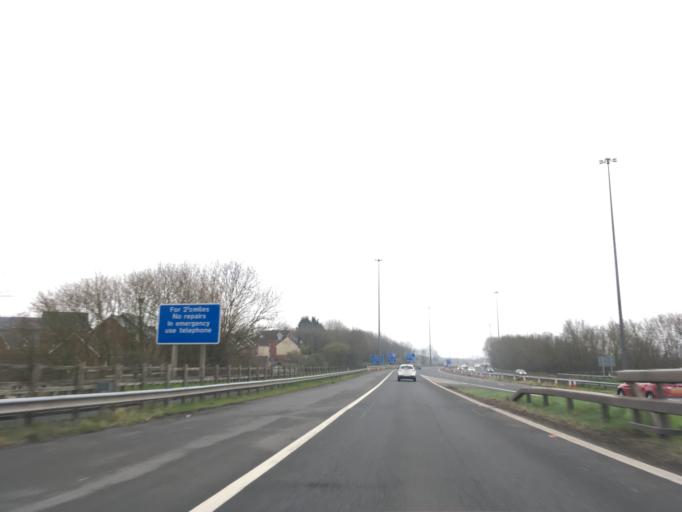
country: GB
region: Wales
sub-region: Monmouthshire
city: Chepstow
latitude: 51.6206
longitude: -2.6695
